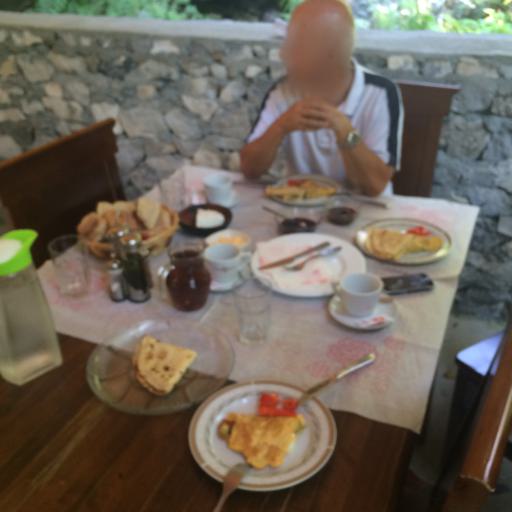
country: AL
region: Kukes
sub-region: Rrethi i Tropojes
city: Valbone
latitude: 42.4573
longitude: 19.9233
